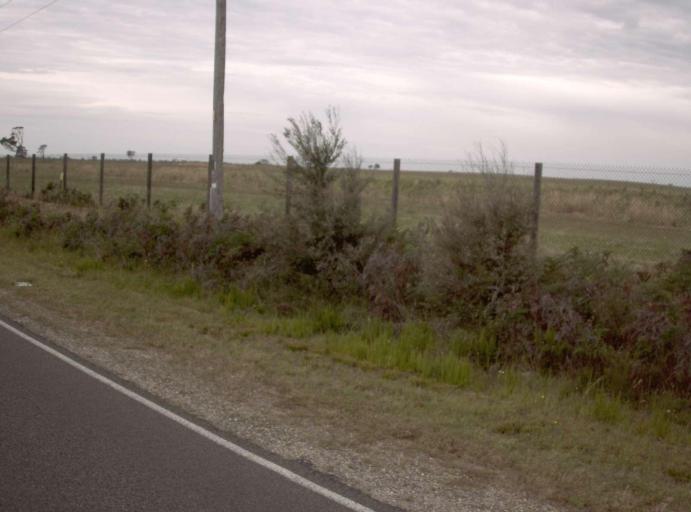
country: AU
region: Victoria
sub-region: Wellington
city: Sale
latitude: -38.1819
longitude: 147.2491
